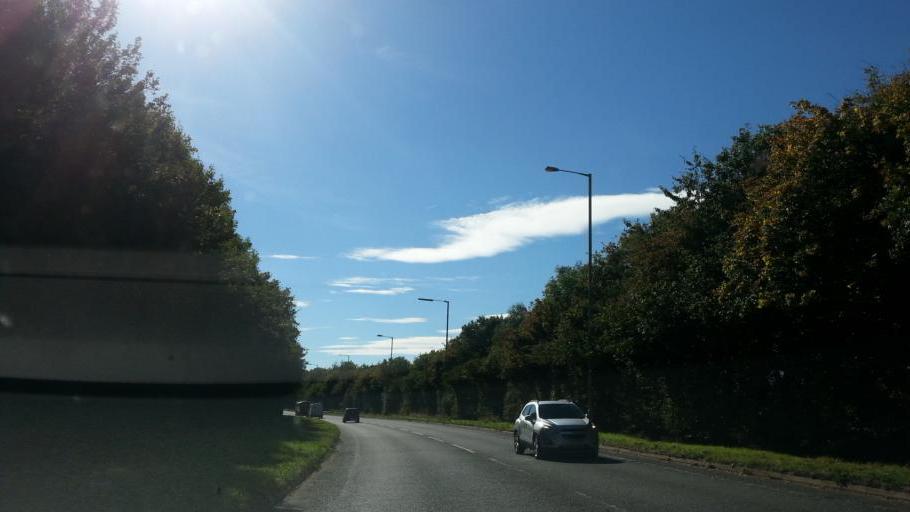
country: GB
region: England
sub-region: Telford and Wrekin
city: Newport
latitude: 52.7595
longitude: -2.3702
